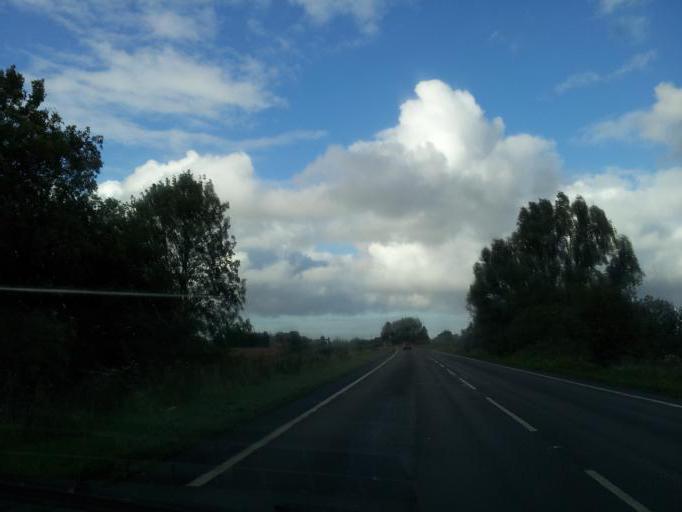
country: GB
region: England
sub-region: Norfolk
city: Terrington St Clement
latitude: 52.7465
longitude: 0.2862
